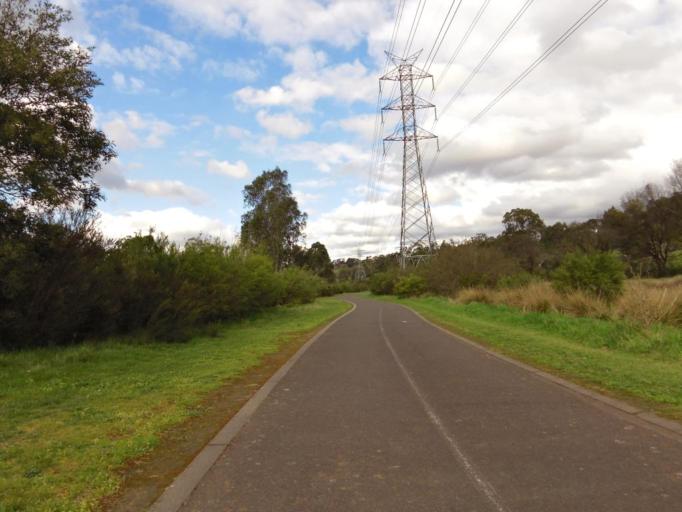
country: AU
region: Victoria
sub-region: Banyule
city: Darch
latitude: -37.7418
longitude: 145.1286
